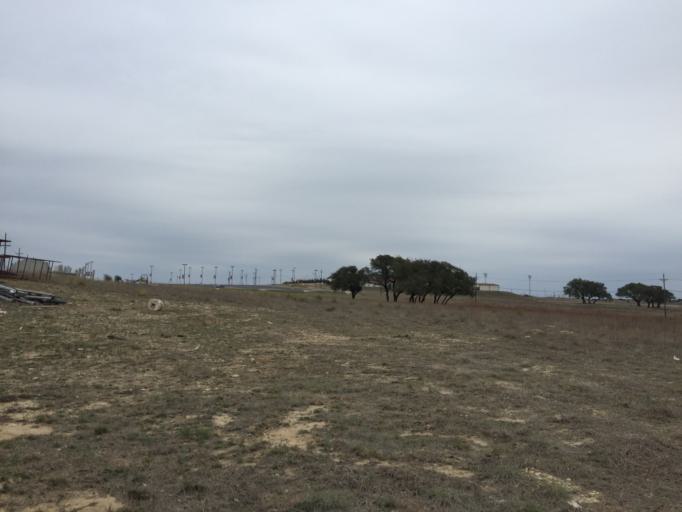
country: US
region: Texas
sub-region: Bell County
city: Fort Hood
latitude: 31.1178
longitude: -97.8129
